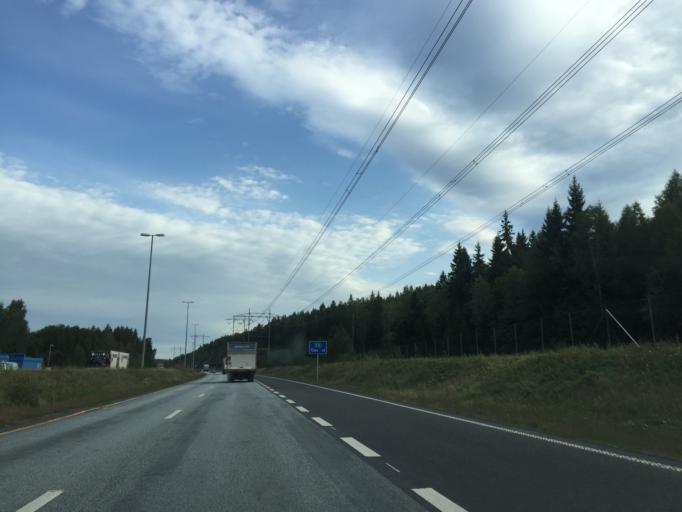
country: NO
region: Akershus
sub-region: Oppegard
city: Kolbotn
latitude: 59.7982
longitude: 10.8432
